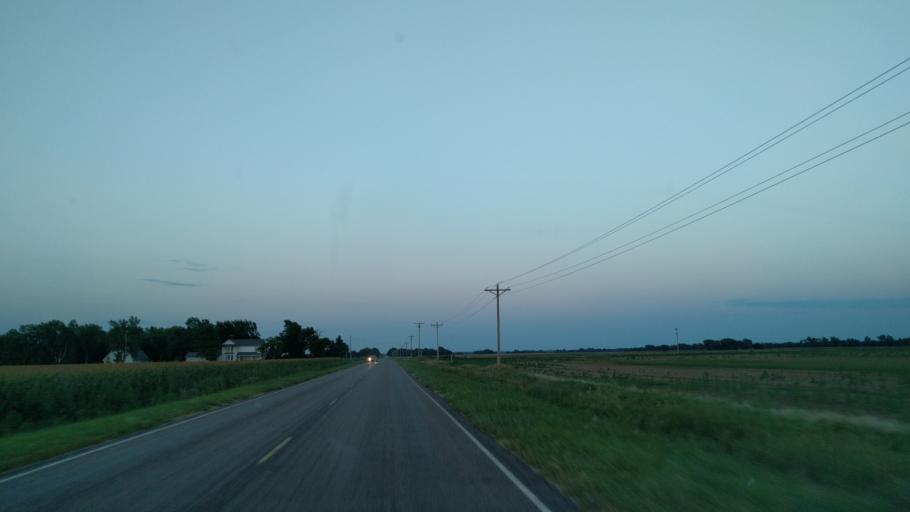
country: US
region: Kansas
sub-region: Rice County
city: Sterling
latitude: 38.2176
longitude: -98.1451
